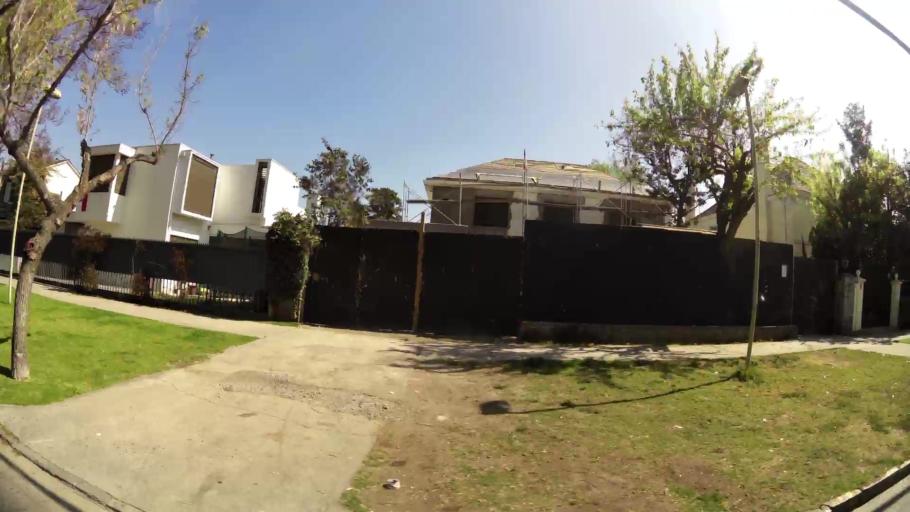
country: CL
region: Santiago Metropolitan
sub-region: Provincia de Santiago
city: Villa Presidente Frei, Nunoa, Santiago, Chile
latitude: -33.4209
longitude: -70.5847
